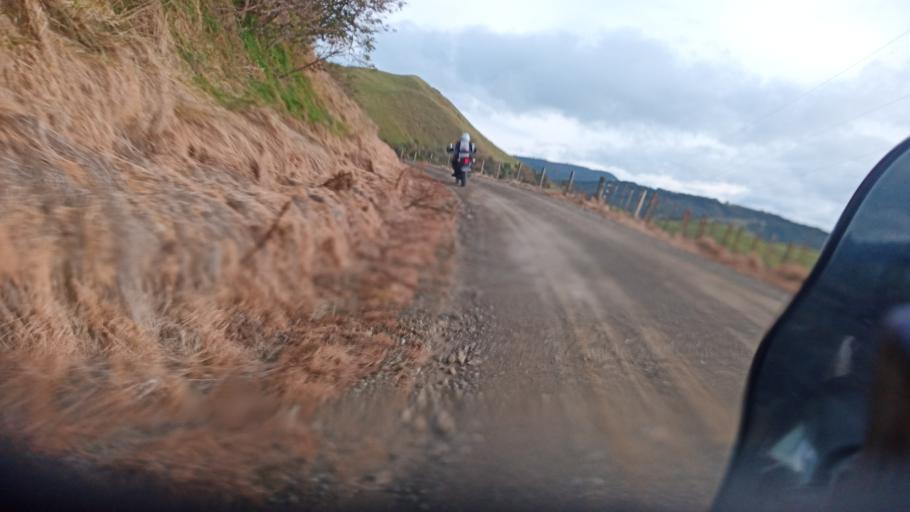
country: NZ
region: Gisborne
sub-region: Gisborne District
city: Gisborne
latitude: -38.4746
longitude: 177.5192
